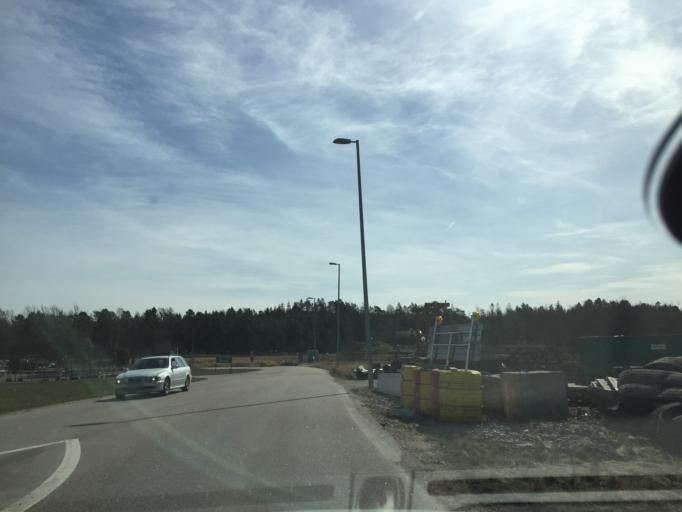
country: SE
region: Vaestra Goetaland
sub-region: Uddevalla Kommun
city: Uddevalla
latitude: 58.3504
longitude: 11.8039
